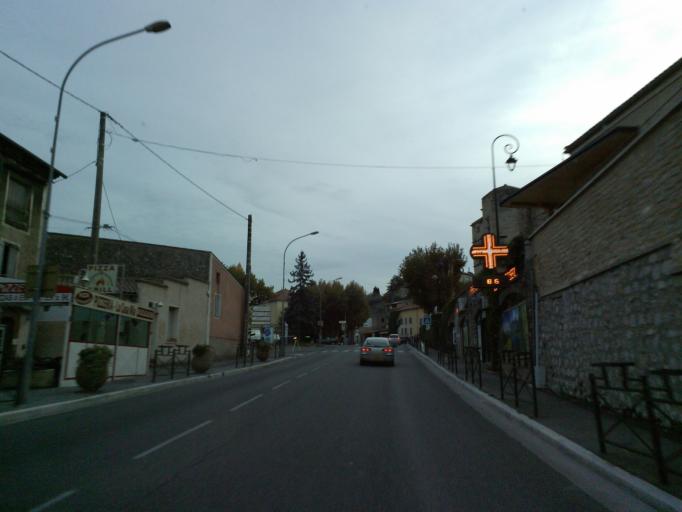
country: FR
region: Provence-Alpes-Cote d'Azur
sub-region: Departement des Alpes-de-Haute-Provence
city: Volonne
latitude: 44.0939
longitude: 6.0098
